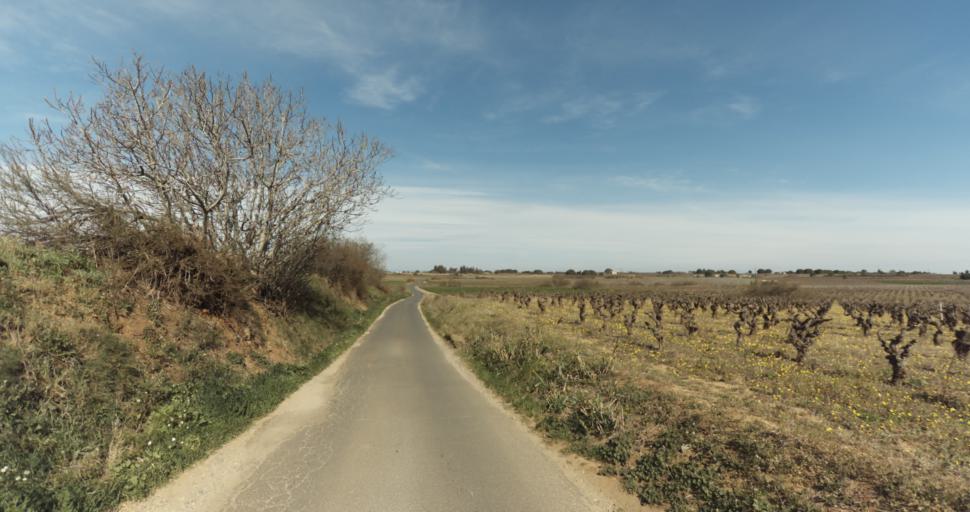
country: FR
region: Languedoc-Roussillon
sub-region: Departement de l'Herault
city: Marseillan
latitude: 43.3386
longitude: 3.5130
